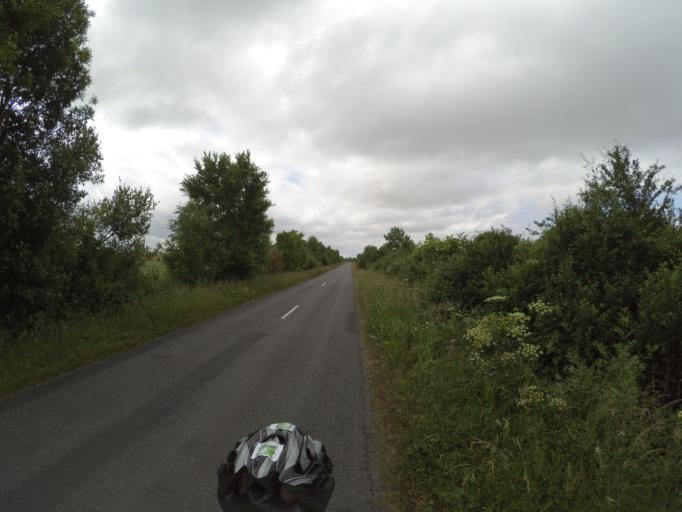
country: FR
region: Poitou-Charentes
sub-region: Departement de la Charente-Maritime
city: Yves
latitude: 46.0342
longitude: -1.0467
